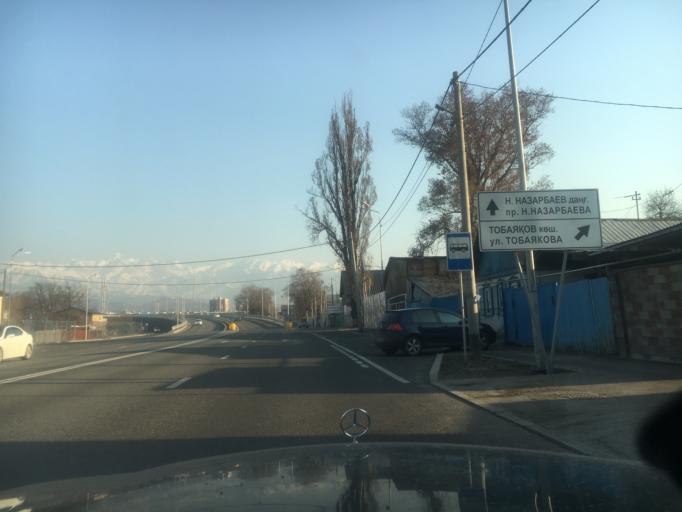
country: KZ
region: Almaty Qalasy
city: Almaty
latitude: 43.2798
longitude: 76.9401
